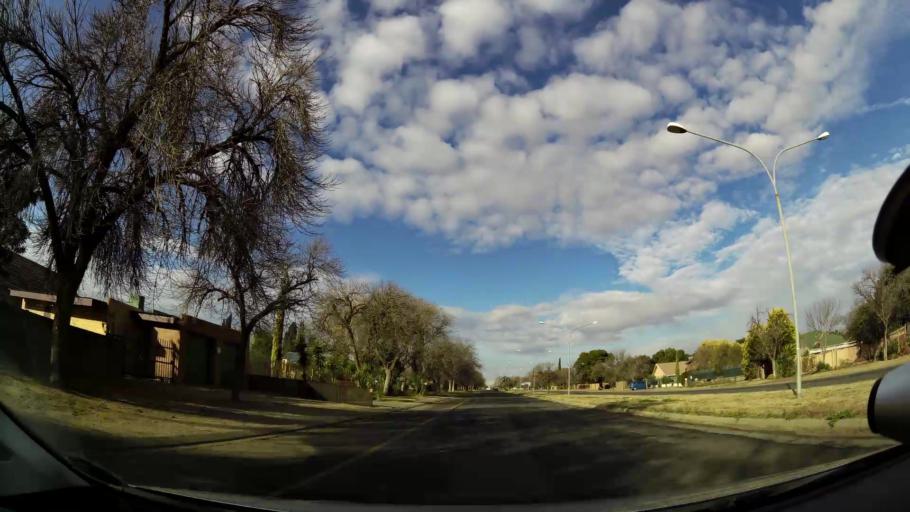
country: ZA
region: Orange Free State
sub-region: Lejweleputswa District Municipality
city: Welkom
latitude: -27.9824
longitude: 26.7221
